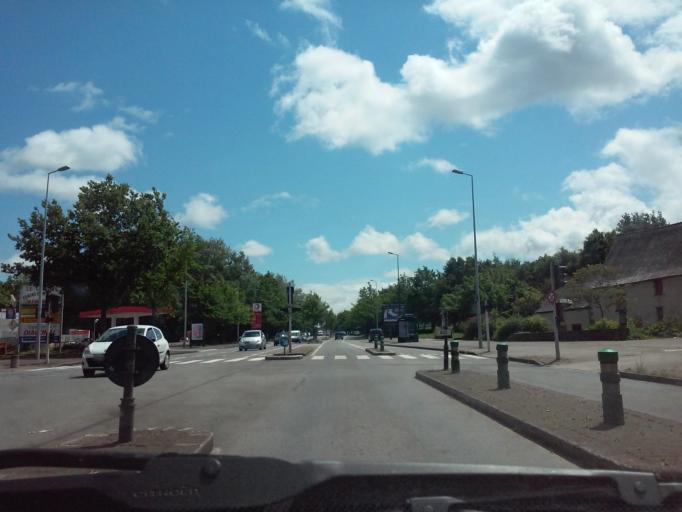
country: FR
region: Brittany
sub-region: Departement d'Ille-et-Vilaine
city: Chantepie
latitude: 48.0974
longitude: -1.6423
